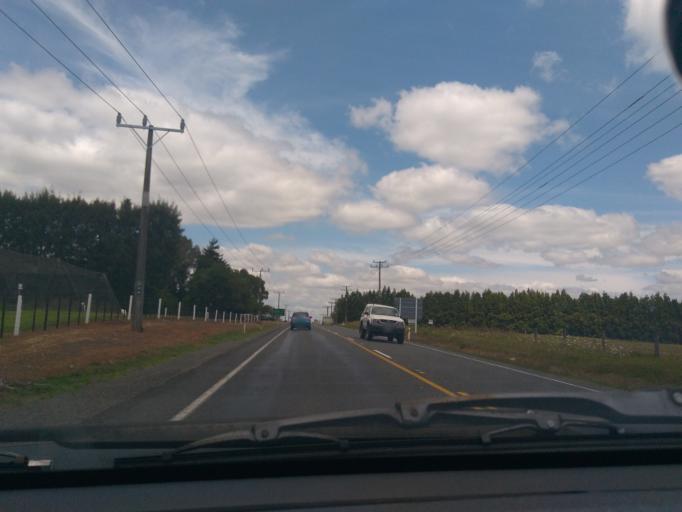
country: NZ
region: Northland
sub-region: Far North District
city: Kerikeri
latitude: -35.2037
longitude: 173.9143
